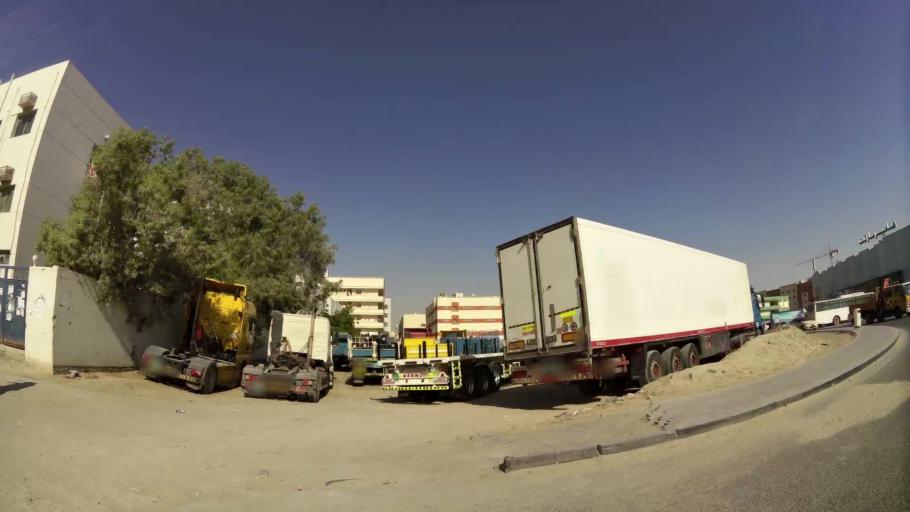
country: AE
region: Dubai
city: Dubai
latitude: 25.0075
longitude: 55.1068
